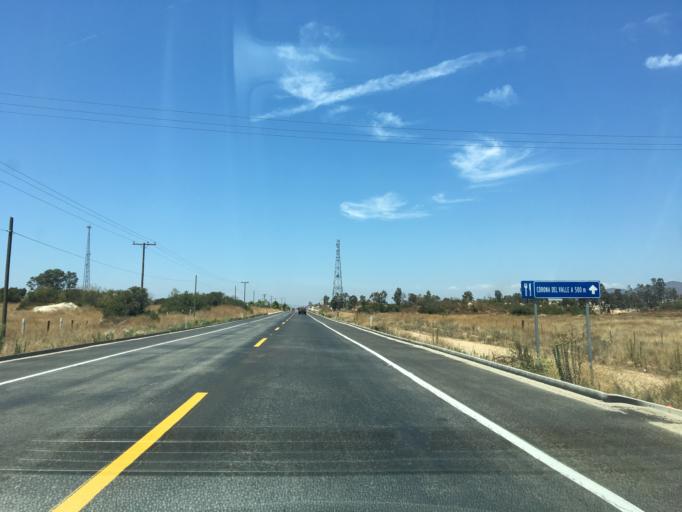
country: MX
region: Baja California
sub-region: Ensenada
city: Rancho Verde
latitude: 32.0120
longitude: -116.6312
